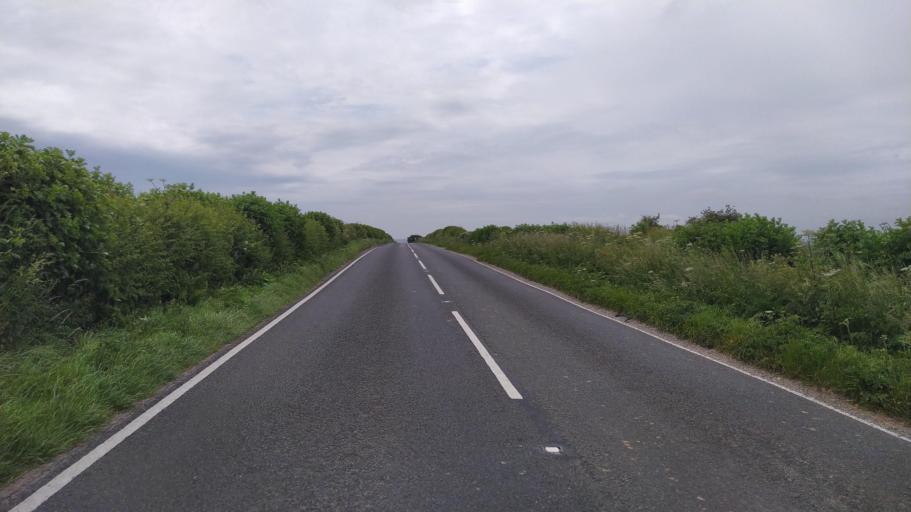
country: GB
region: England
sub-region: Dorset
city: Dorchester
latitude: 50.7939
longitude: -2.4538
